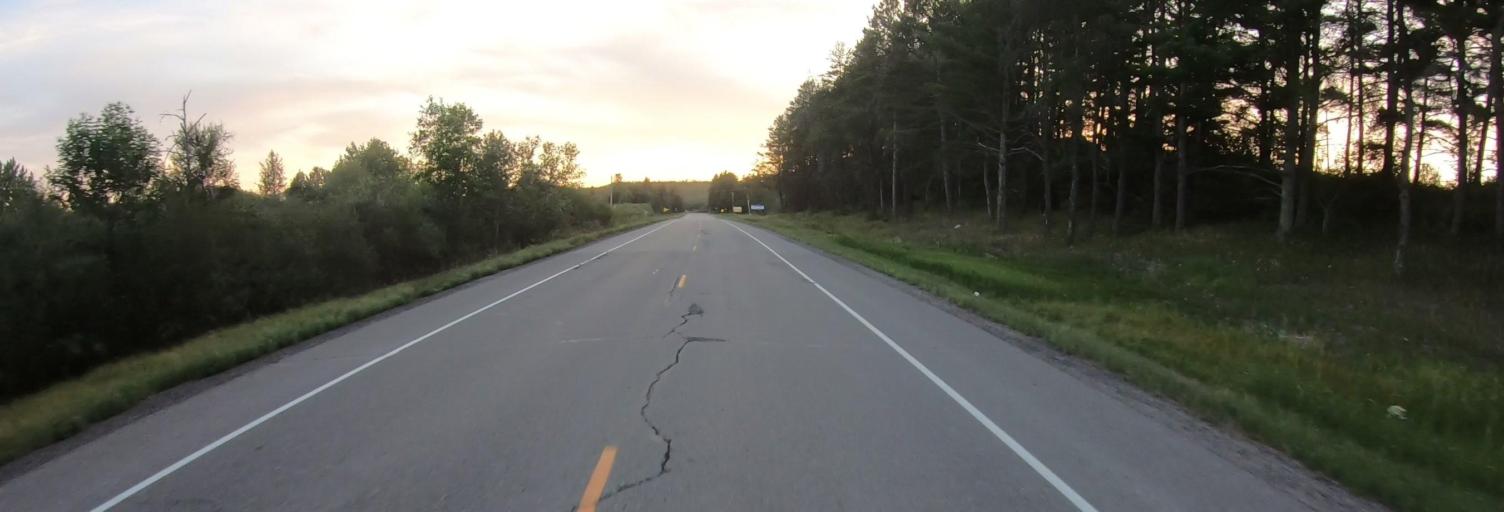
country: US
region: Minnesota
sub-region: Saint Louis County
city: Aurora
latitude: 47.8128
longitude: -92.2412
